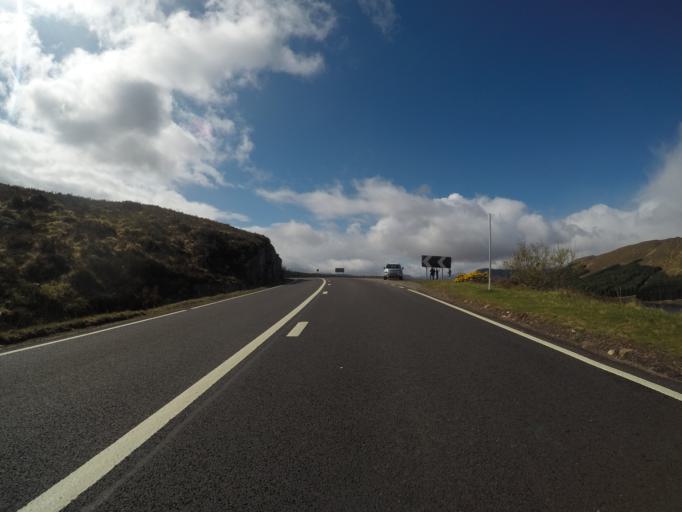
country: GB
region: Scotland
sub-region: Highland
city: Spean Bridge
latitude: 57.1154
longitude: -4.9831
